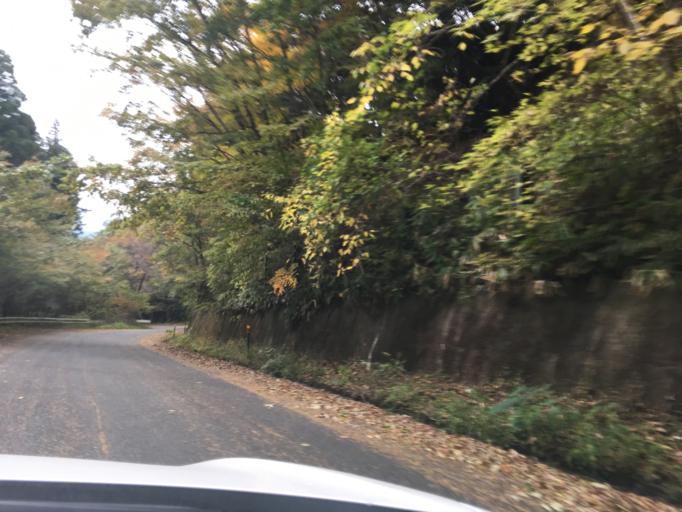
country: JP
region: Fukushima
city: Iwaki
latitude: 37.0984
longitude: 140.7863
